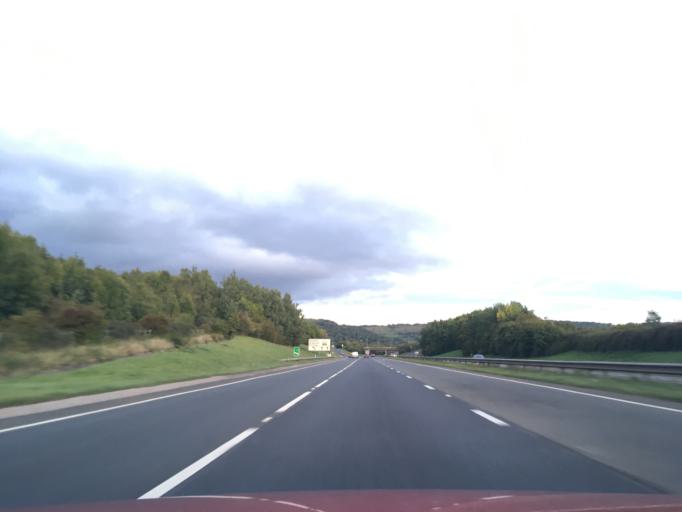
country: GB
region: England
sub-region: Gloucestershire
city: Shurdington
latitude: 51.8523
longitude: -2.1477
